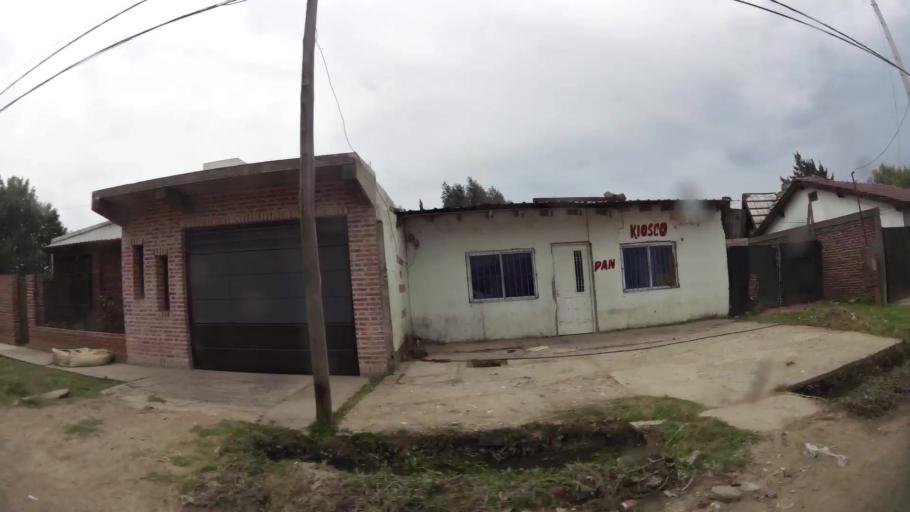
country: AR
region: Buenos Aires
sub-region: Partido de Zarate
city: Zarate
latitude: -34.1101
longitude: -59.0421
